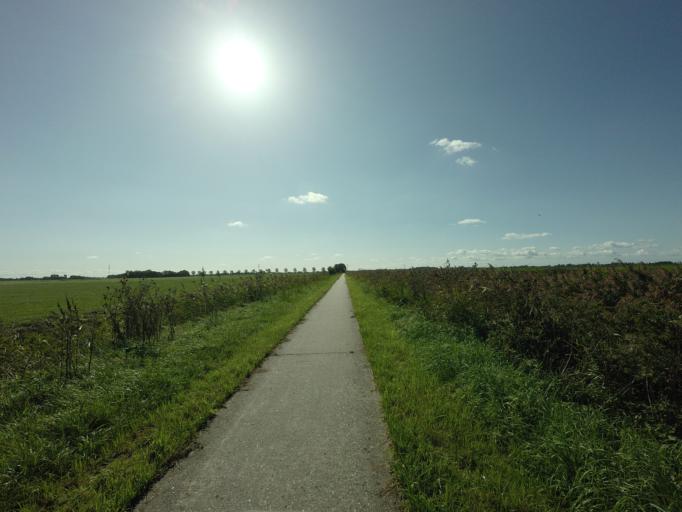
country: NL
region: Friesland
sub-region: Gemeente Boarnsterhim
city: Reduzum
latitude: 53.1246
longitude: 5.7547
